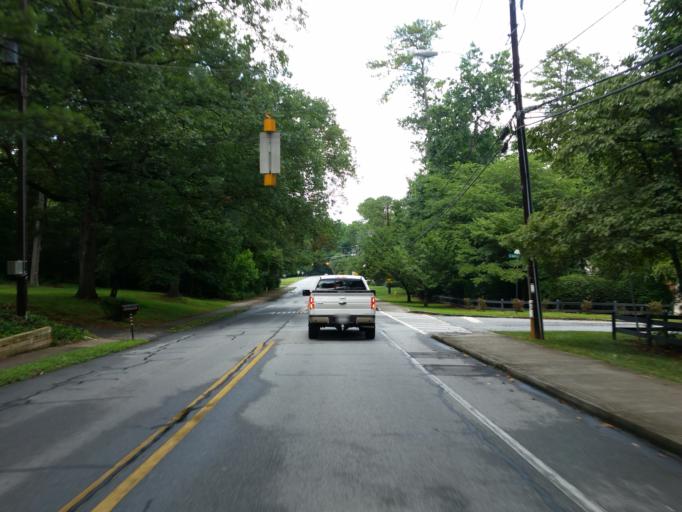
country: US
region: Georgia
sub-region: DeKalb County
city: Dunwoody
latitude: 33.9580
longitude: -84.3422
